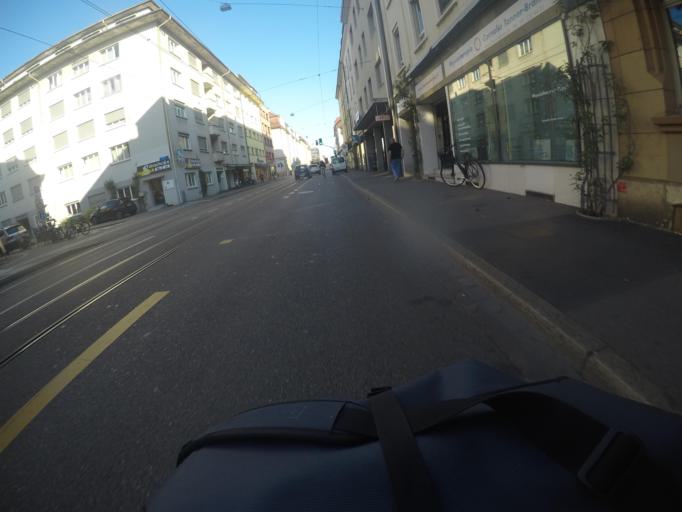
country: CH
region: Basel-City
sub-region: Basel-Stadt
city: Basel
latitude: 47.5689
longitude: 7.5798
